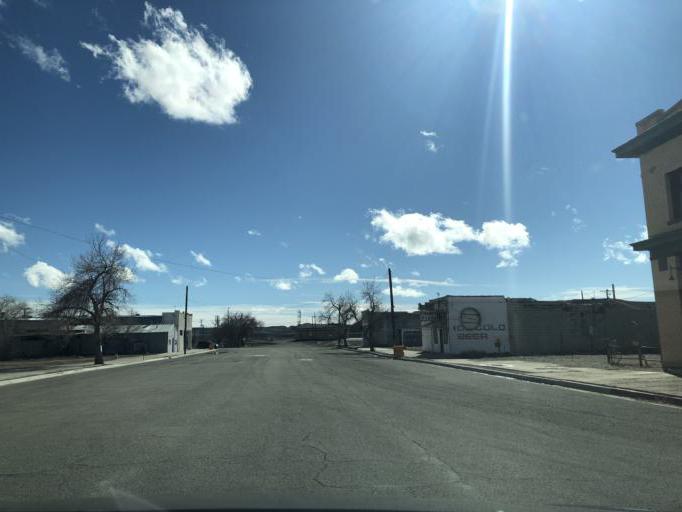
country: US
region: Utah
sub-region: Carbon County
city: East Carbon City
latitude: 38.9943
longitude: -110.1652
